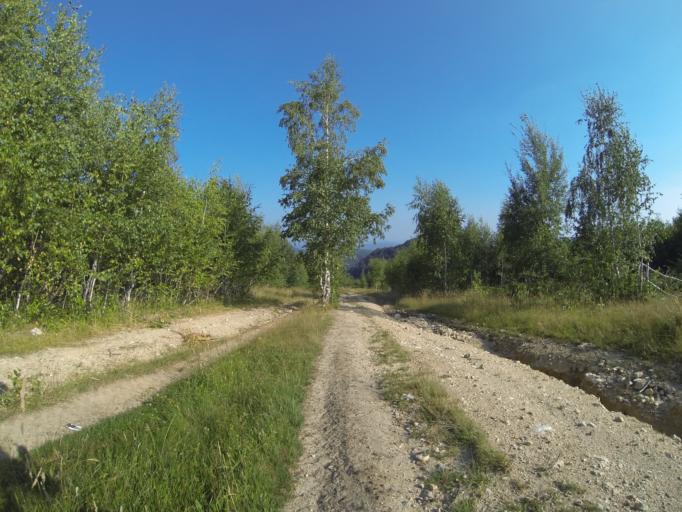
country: RO
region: Valcea
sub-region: Comuna Vaideeni
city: Vaideeni
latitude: 45.2001
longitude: 23.9806
